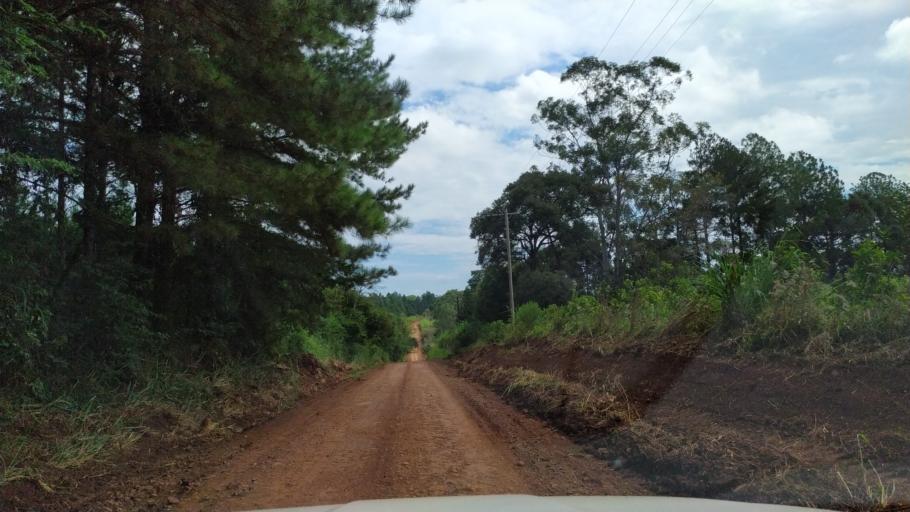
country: AR
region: Misiones
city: Puerto Piray
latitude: -26.5349
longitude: -54.6399
